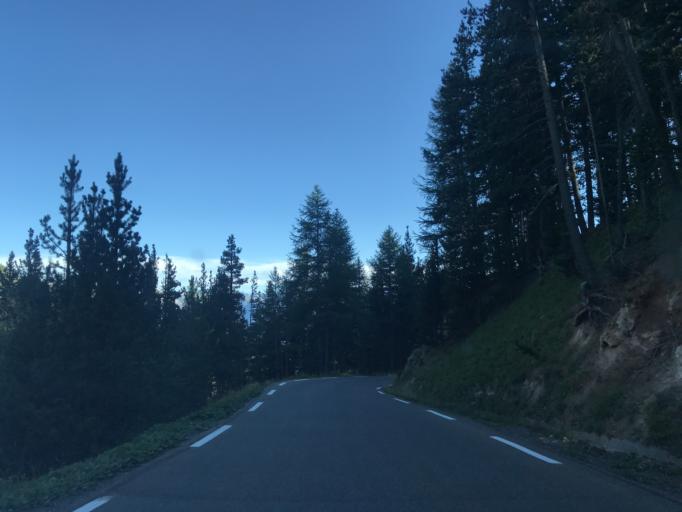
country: FR
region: Provence-Alpes-Cote d'Azur
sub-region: Departement des Hautes-Alpes
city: Villar-Saint-Pancrace
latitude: 44.8047
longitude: 6.7343
